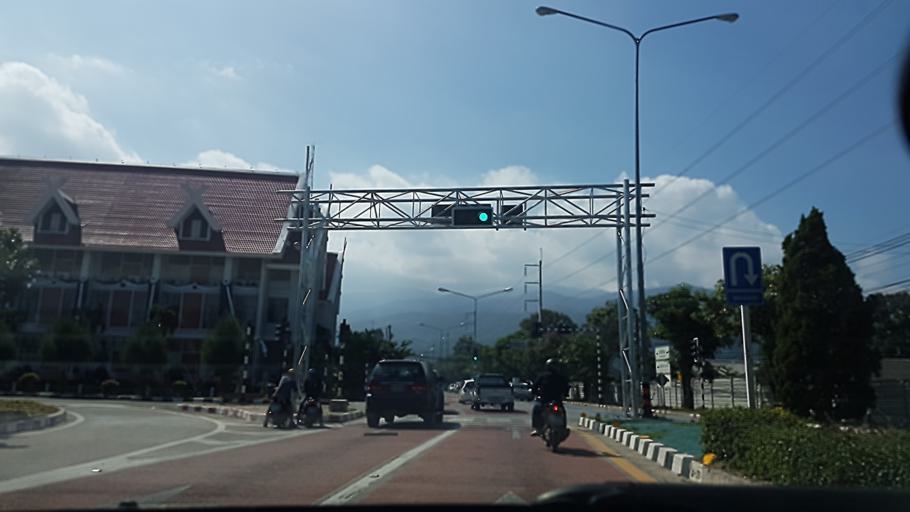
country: TH
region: Chiang Mai
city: Chiang Mai
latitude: 18.8420
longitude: 98.9715
